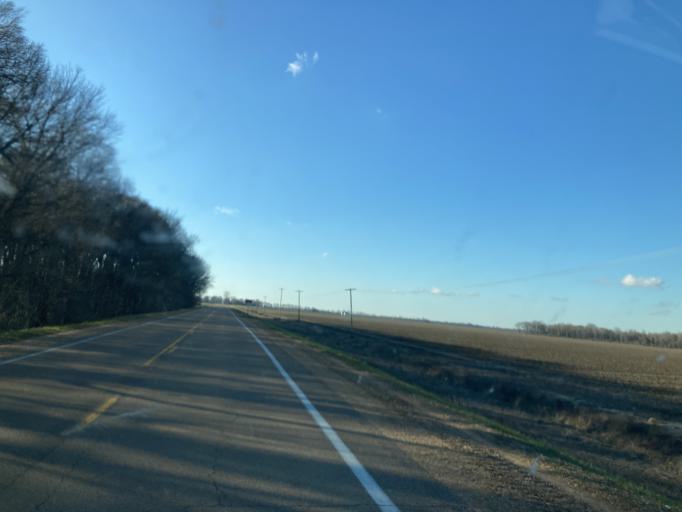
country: US
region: Mississippi
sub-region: Yazoo County
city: Yazoo City
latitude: 32.9246
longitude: -90.5709
